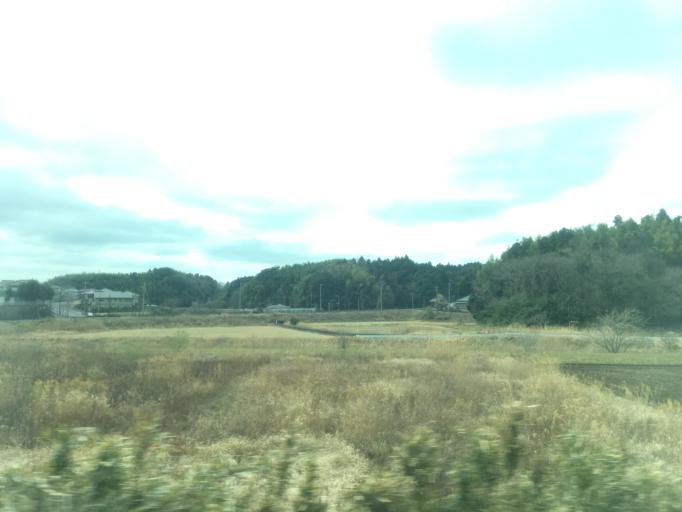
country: JP
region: Chiba
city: Narita
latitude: 35.7889
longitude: 140.3014
